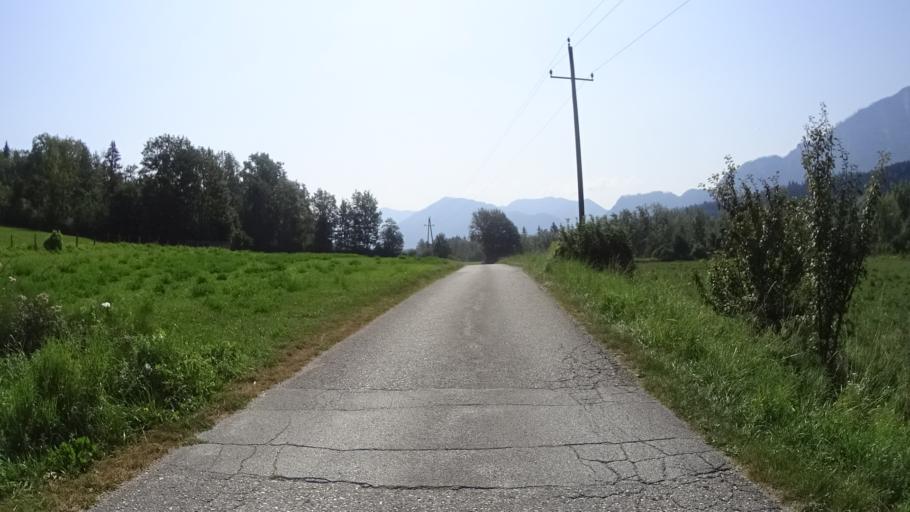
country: AT
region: Carinthia
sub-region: Politischer Bezirk Volkermarkt
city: Gallizien
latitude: 46.5660
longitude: 14.5321
